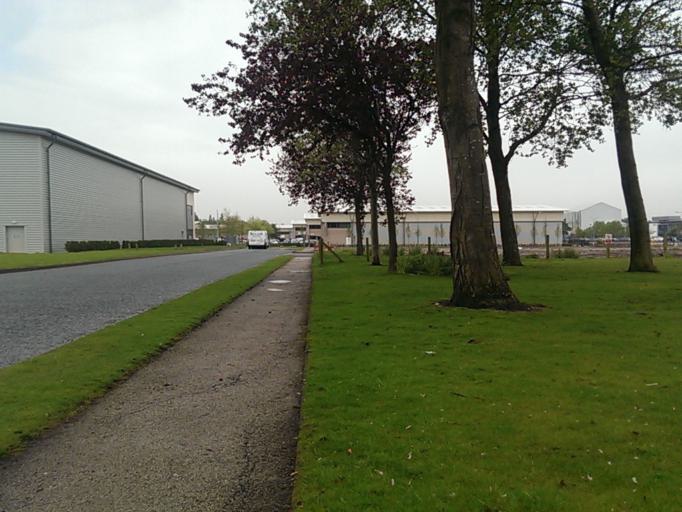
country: GB
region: England
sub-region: Warrington
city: Culcheth
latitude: 53.4270
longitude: -2.5201
